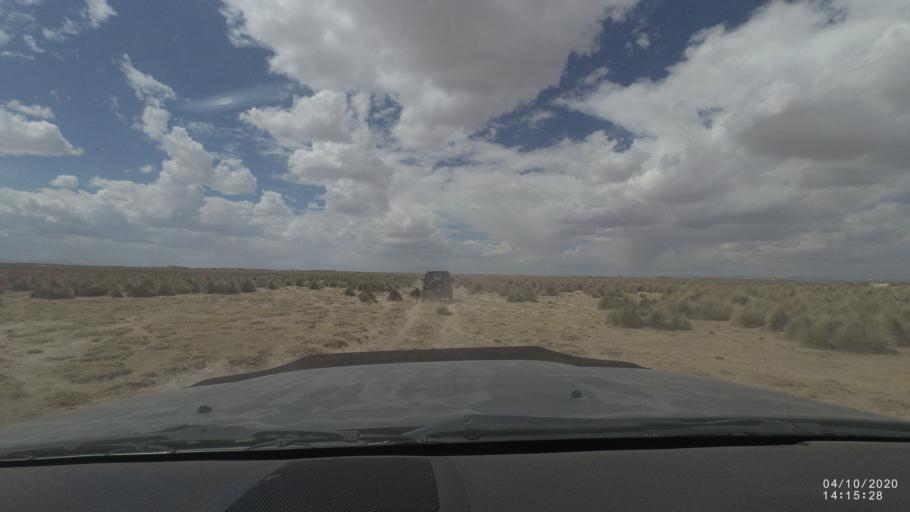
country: BO
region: Oruro
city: Poopo
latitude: -18.6930
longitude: -67.4538
